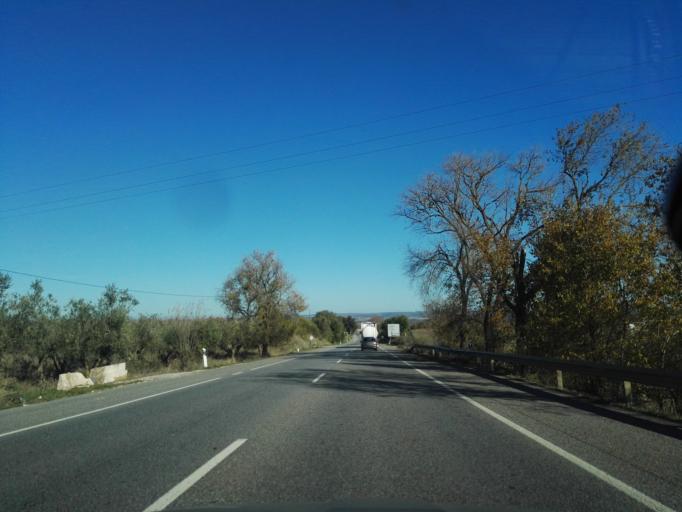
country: PT
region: Evora
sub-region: Borba
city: Borba
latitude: 38.8119
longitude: -7.4537
